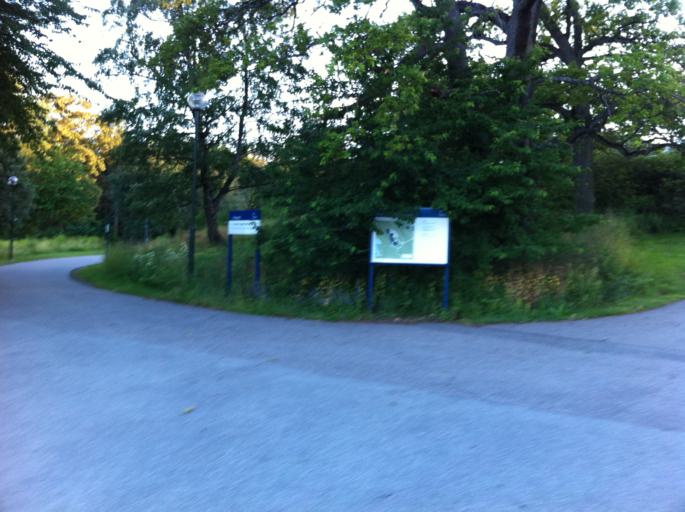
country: SE
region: Stockholm
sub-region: Norrtalje Kommun
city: Bergshamra
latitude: 59.3676
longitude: 18.0442
